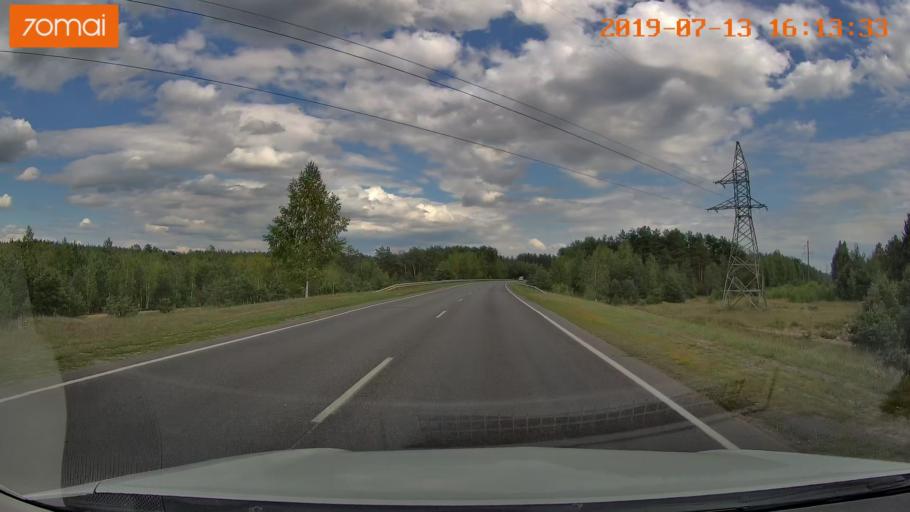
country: BY
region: Mogilev
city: Babruysk
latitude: 53.1623
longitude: 29.3060
